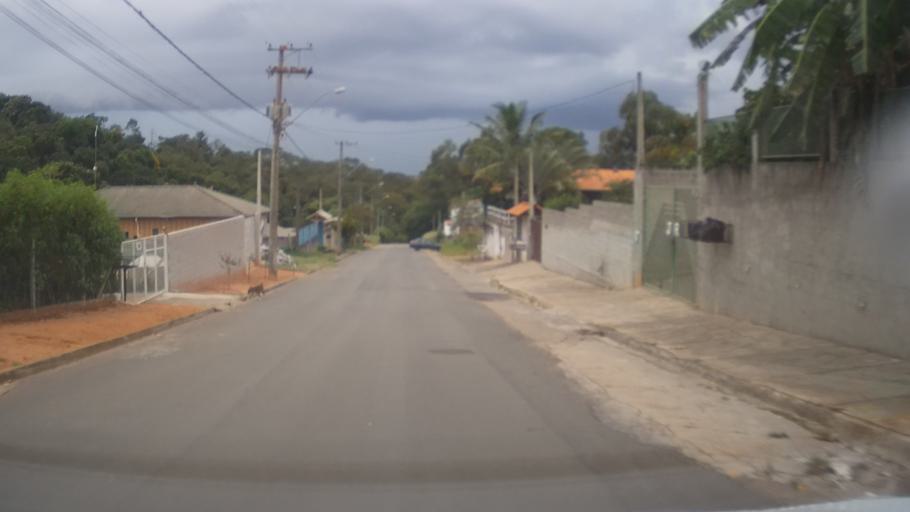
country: BR
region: Sao Paulo
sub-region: Itupeva
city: Itupeva
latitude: -23.1931
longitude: -47.0671
